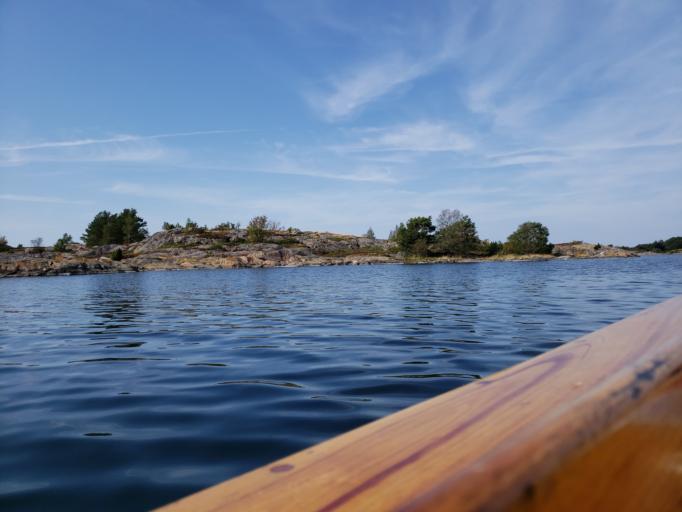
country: FI
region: Varsinais-Suomi
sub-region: Aboland-Turunmaa
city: Dragsfjaerd
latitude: 59.8437
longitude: 22.2057
